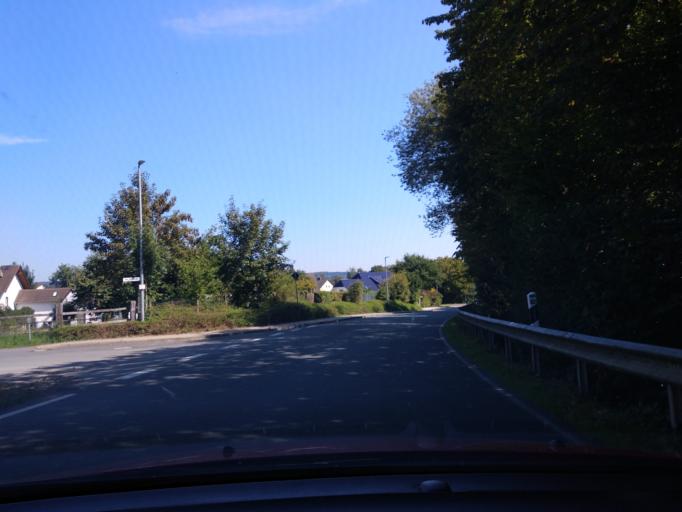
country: DE
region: North Rhine-Westphalia
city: Beverungen
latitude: 51.6717
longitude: 9.3677
